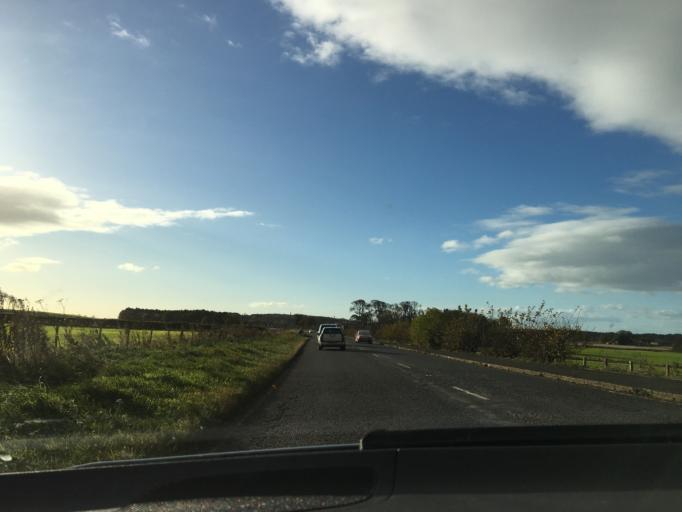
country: GB
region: Scotland
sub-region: East Lothian
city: North Berwick
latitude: 56.0527
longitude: -2.7622
